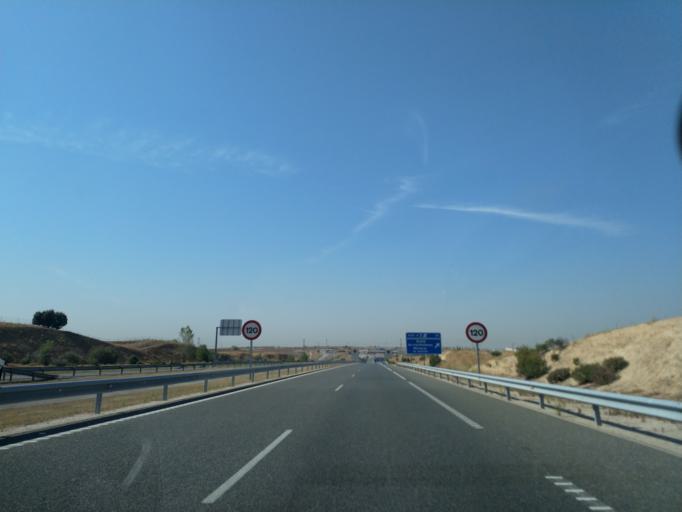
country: ES
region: Madrid
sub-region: Provincia de Madrid
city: Arroyomolinos
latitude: 40.2667
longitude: -3.8987
